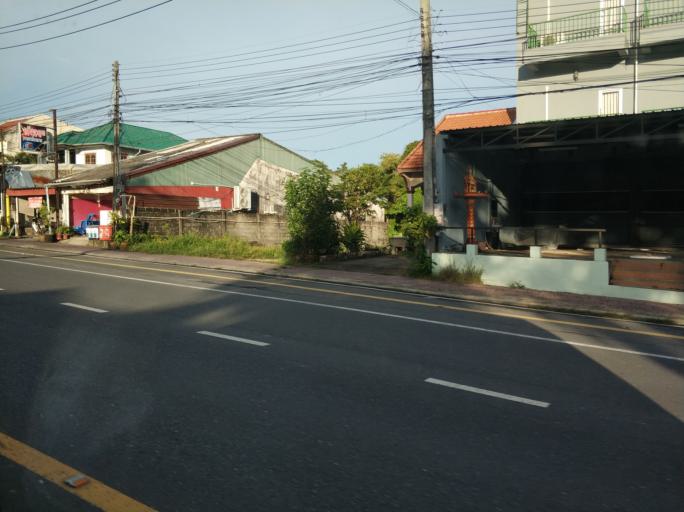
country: TH
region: Phuket
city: Kathu
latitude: 7.9056
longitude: 98.3361
